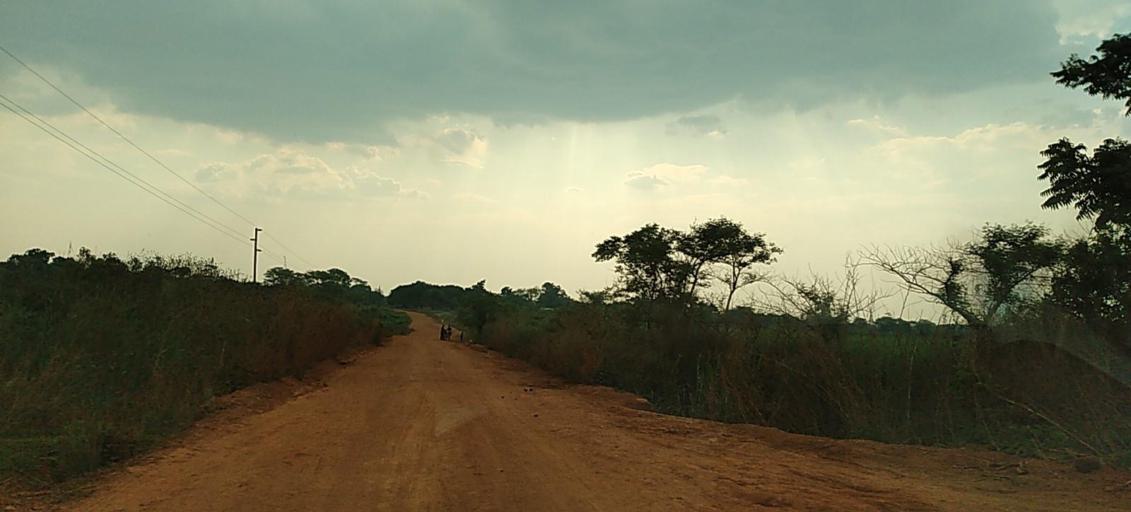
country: ZM
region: Copperbelt
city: Kalulushi
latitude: -12.9376
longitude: 27.9291
